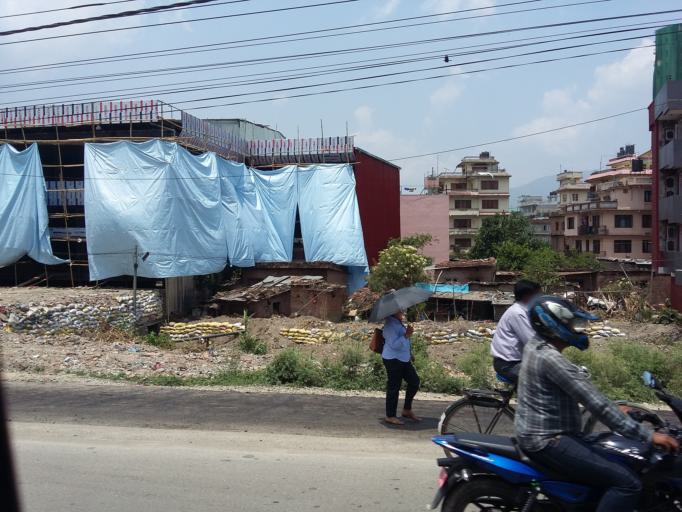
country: NP
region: Central Region
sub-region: Bagmati Zone
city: Kathmandu
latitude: 27.7380
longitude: 85.3249
